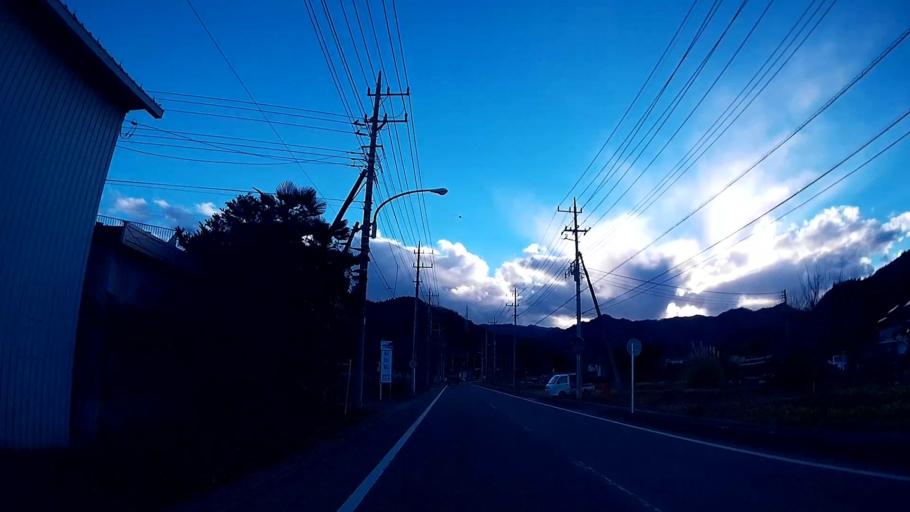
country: JP
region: Saitama
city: Chichibu
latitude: 36.0244
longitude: 138.9851
